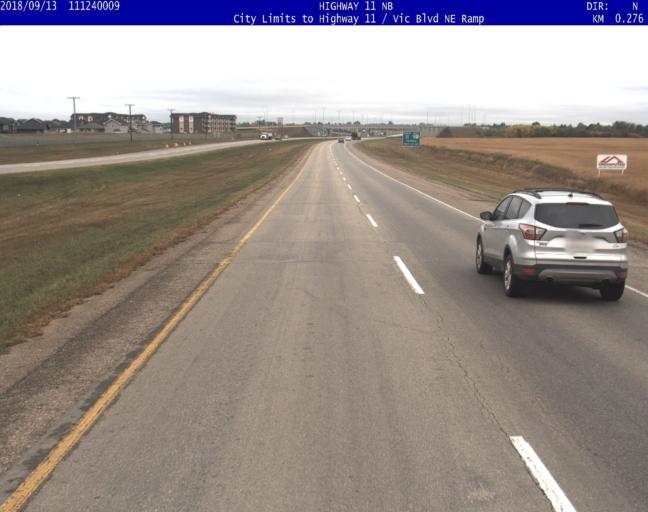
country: CA
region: Saskatchewan
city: Saskatoon
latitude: 52.0723
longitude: -106.6036
